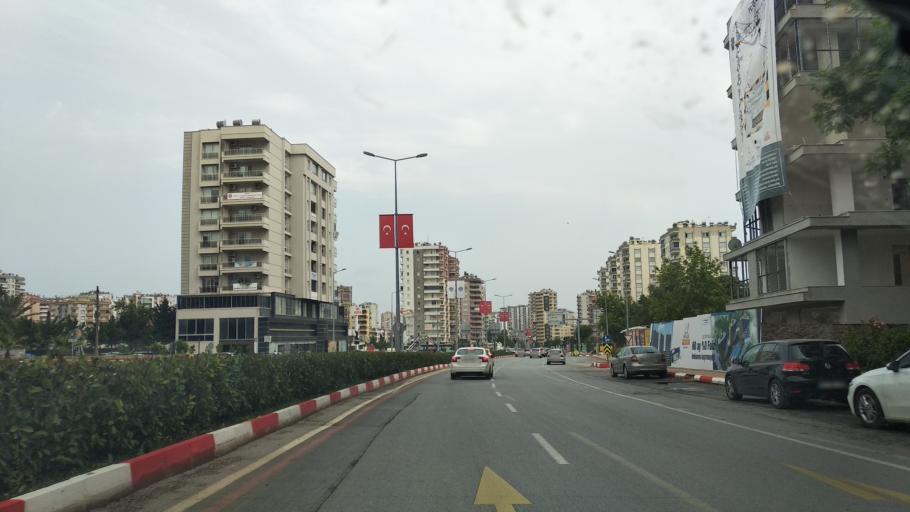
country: TR
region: Mersin
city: Mercin
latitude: 36.7961
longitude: 34.5967
